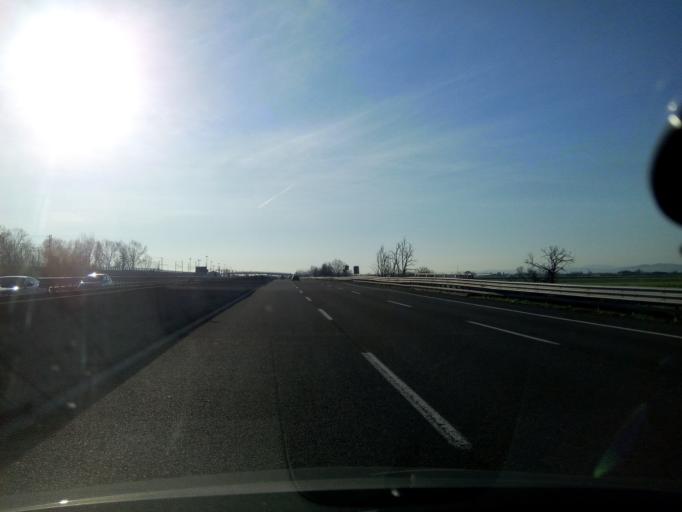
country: IT
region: Emilia-Romagna
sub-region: Provincia di Reggio Emilia
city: Campegine
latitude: 44.7626
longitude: 10.5312
